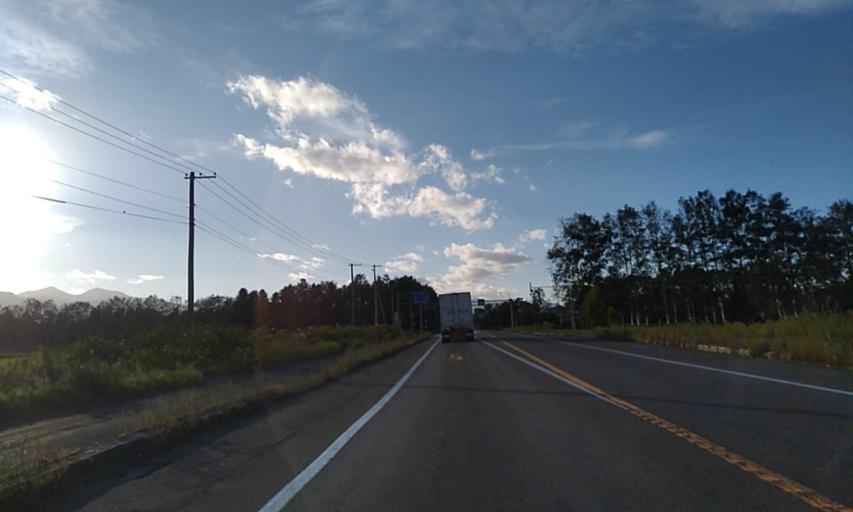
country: JP
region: Hokkaido
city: Otofuke
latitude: 42.9491
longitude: 142.9348
